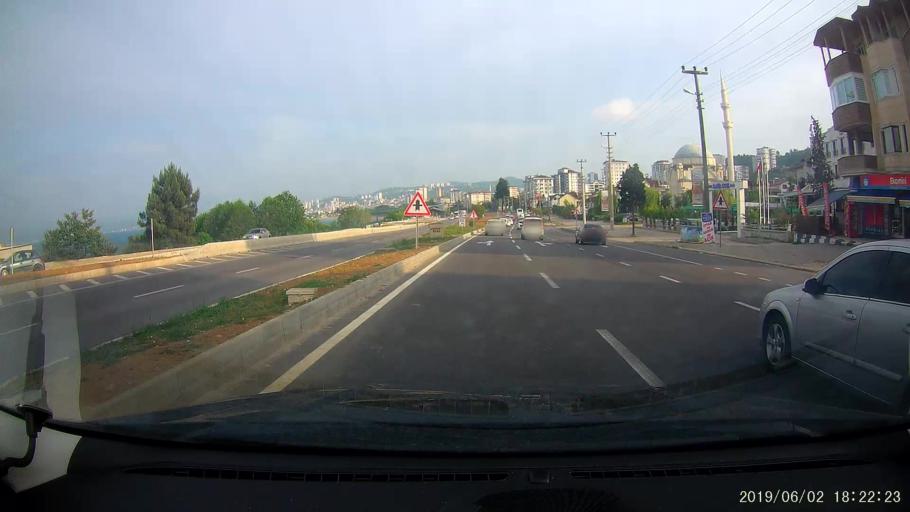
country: TR
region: Ordu
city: Fatsa
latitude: 41.0578
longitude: 37.4770
